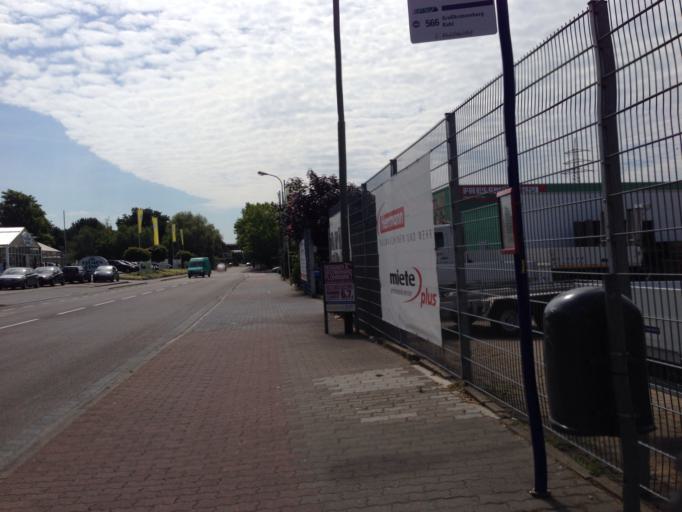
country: DE
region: Hesse
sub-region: Regierungsbezirk Darmstadt
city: Hanau am Main
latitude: 50.1169
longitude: 8.9306
